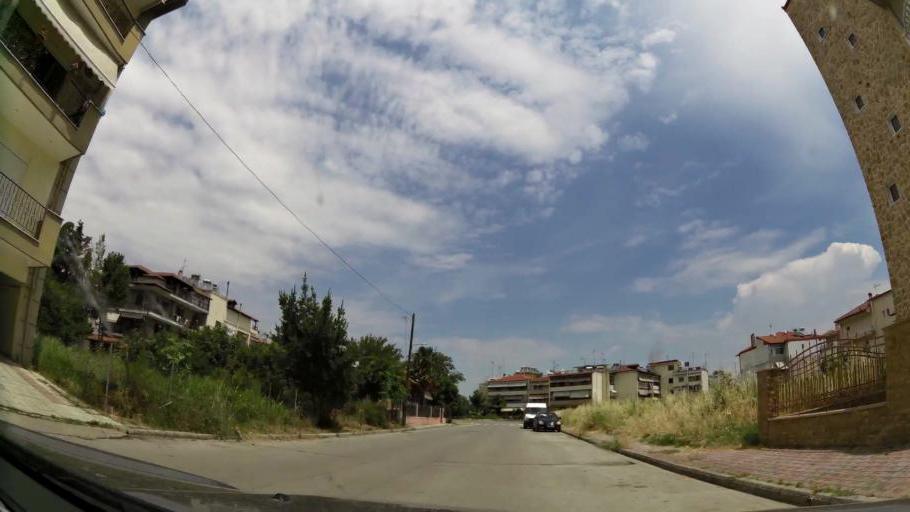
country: GR
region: Central Macedonia
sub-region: Nomos Pierias
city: Katerini
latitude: 40.2722
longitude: 22.5187
